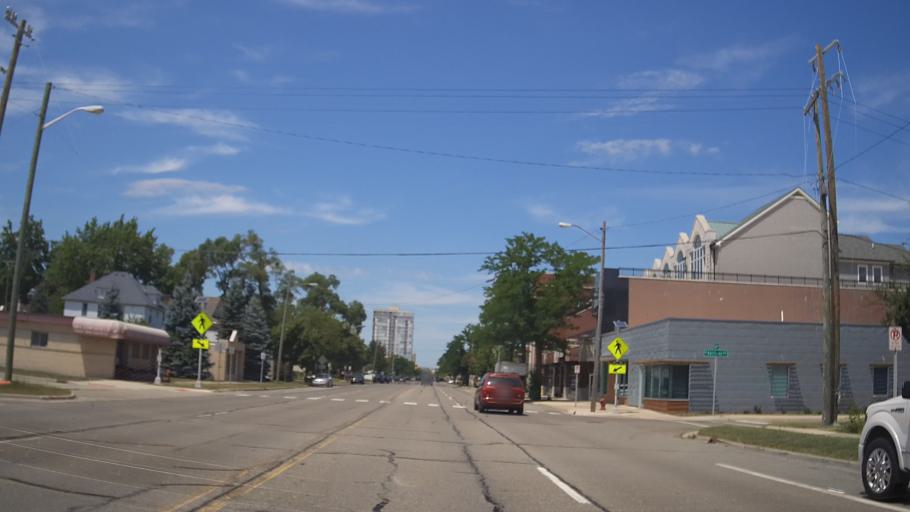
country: US
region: Michigan
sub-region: Oakland County
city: Royal Oak
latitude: 42.4803
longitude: -83.1463
